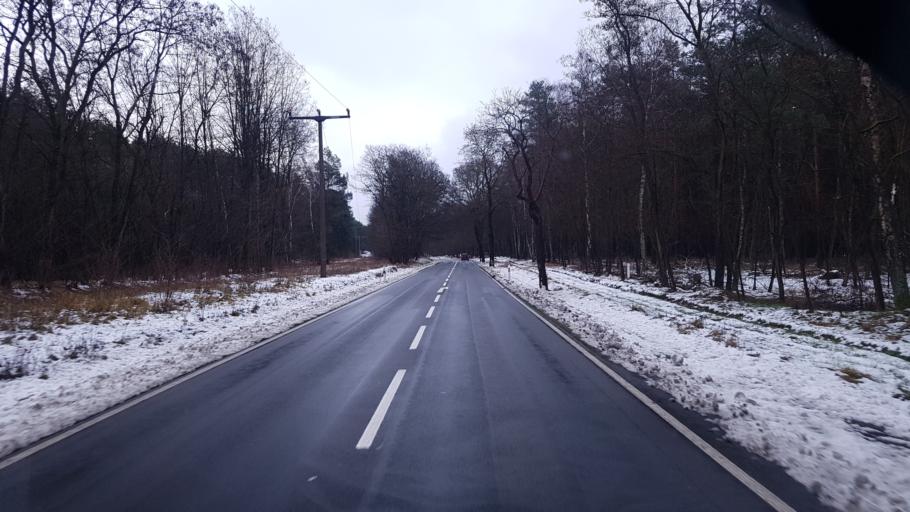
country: DE
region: Brandenburg
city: Jamlitz
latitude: 51.9893
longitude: 14.3773
